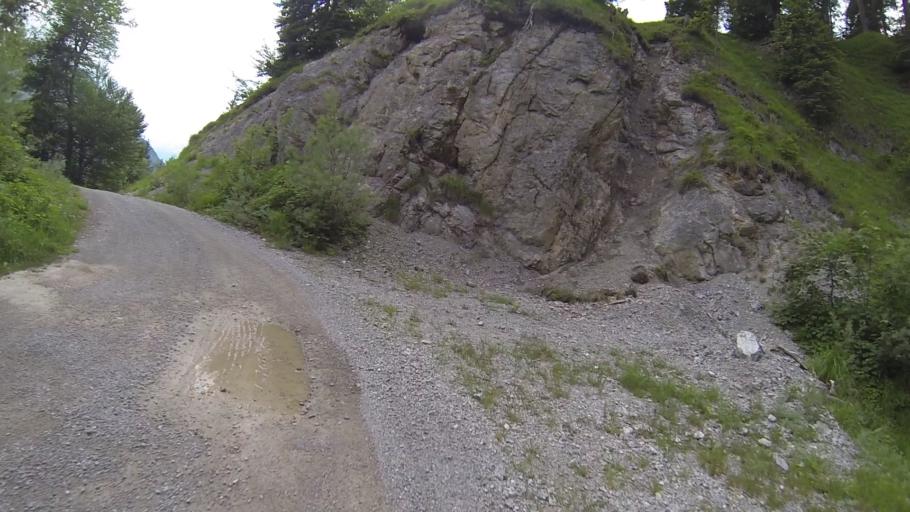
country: AT
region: Tyrol
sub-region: Politischer Bezirk Reutte
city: Breitenwang
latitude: 47.5036
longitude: 10.7554
